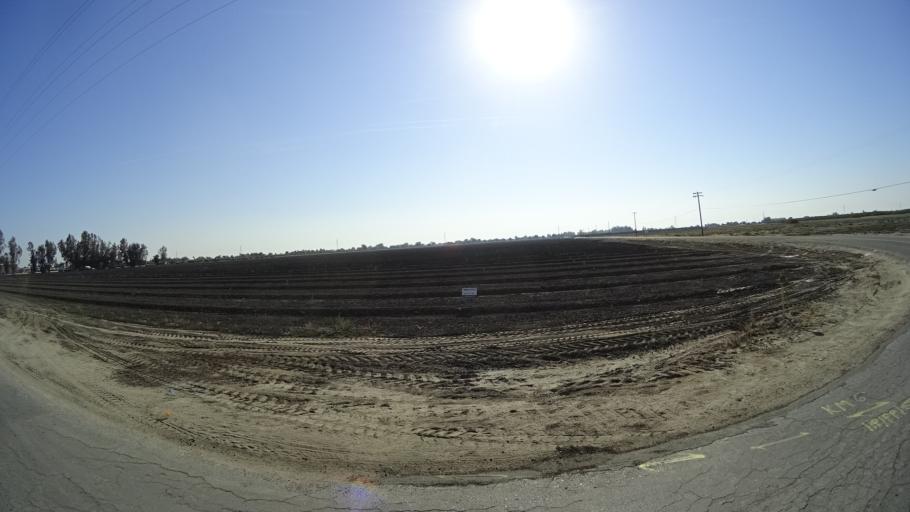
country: US
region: California
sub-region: Fresno County
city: Riverdale
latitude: 36.3768
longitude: -119.9051
